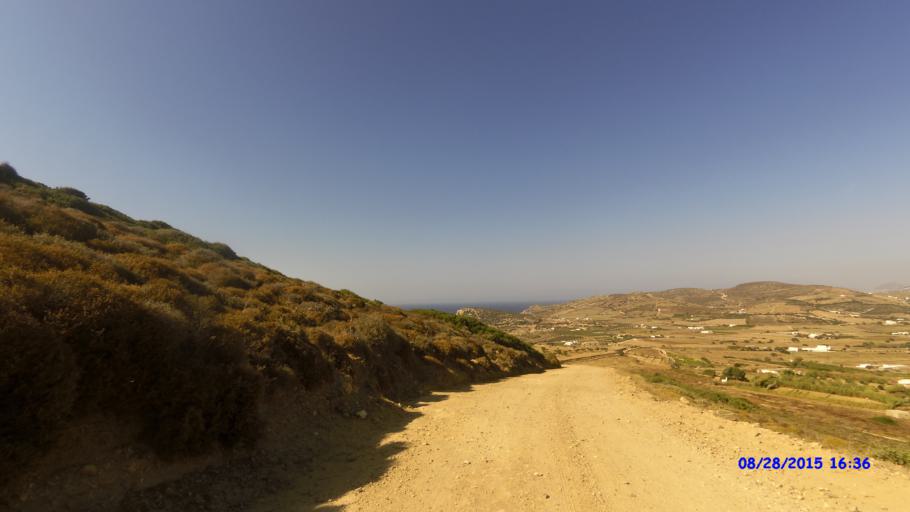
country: GR
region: South Aegean
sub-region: Nomos Kykladon
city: Antiparos
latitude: 37.0086
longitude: 25.0458
